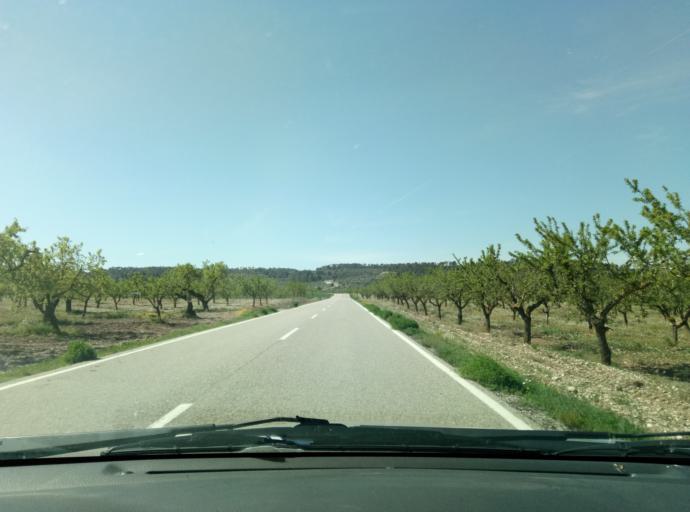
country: ES
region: Catalonia
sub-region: Provincia de Lleida
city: Vallbona de les Monges
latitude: 41.5410
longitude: 1.0285
